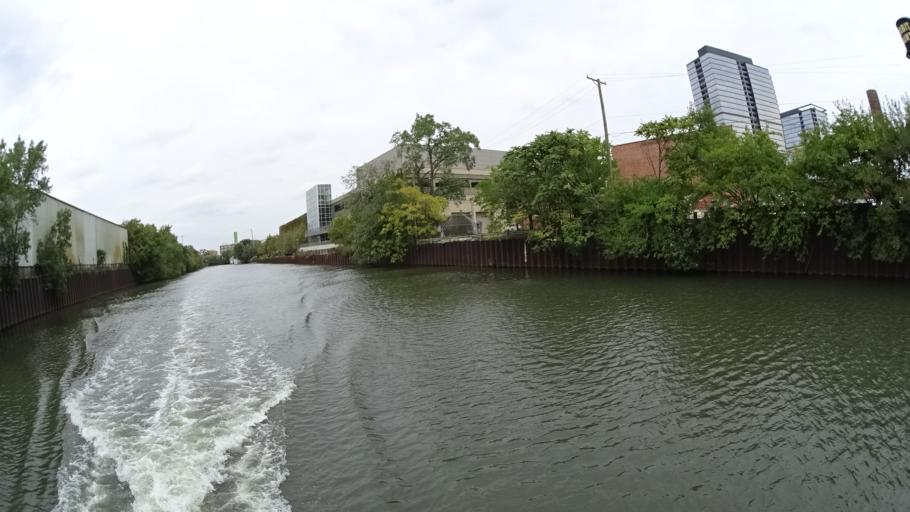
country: US
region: Illinois
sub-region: Cook County
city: Chicago
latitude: 41.9073
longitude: -87.6526
